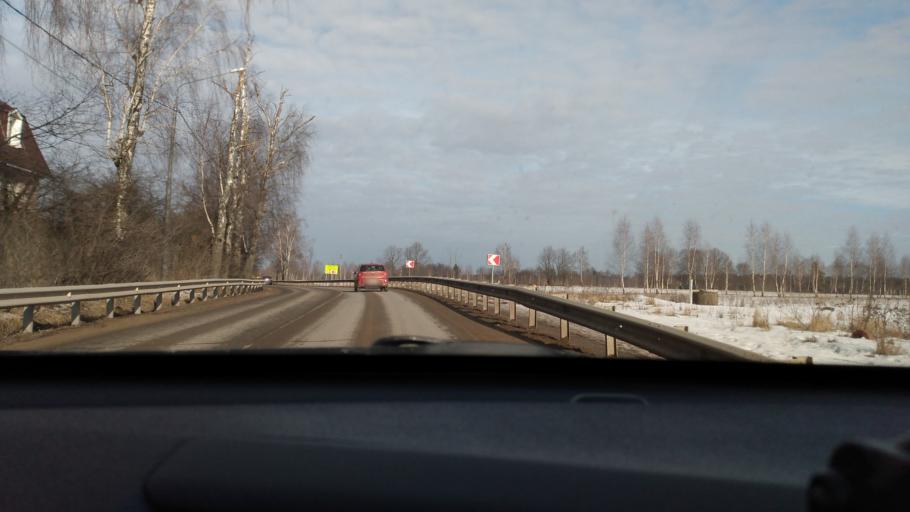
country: RU
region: Moskovskaya
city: Nakhabino
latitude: 55.8591
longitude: 37.1863
